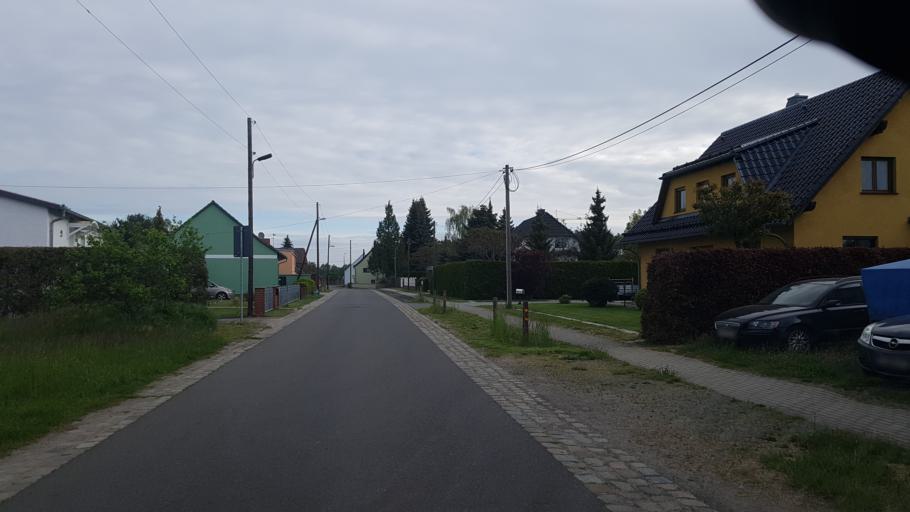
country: DE
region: Brandenburg
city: Luckenwalde
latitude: 52.1118
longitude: 13.1105
